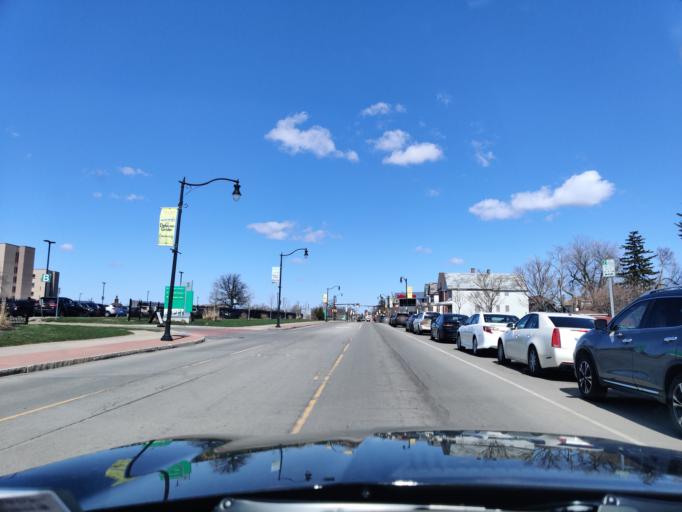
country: US
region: New York
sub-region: Erie County
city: Eggertsville
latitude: 42.9256
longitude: -78.8291
